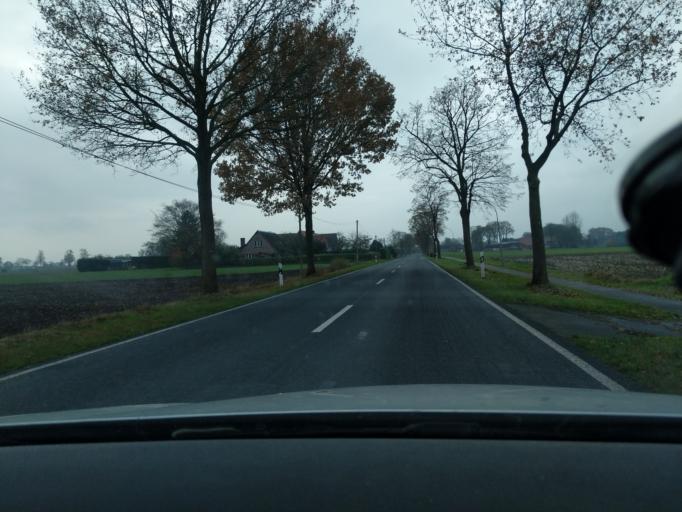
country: DE
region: Lower Saxony
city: Ahlerstedt
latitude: 53.3855
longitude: 9.4757
